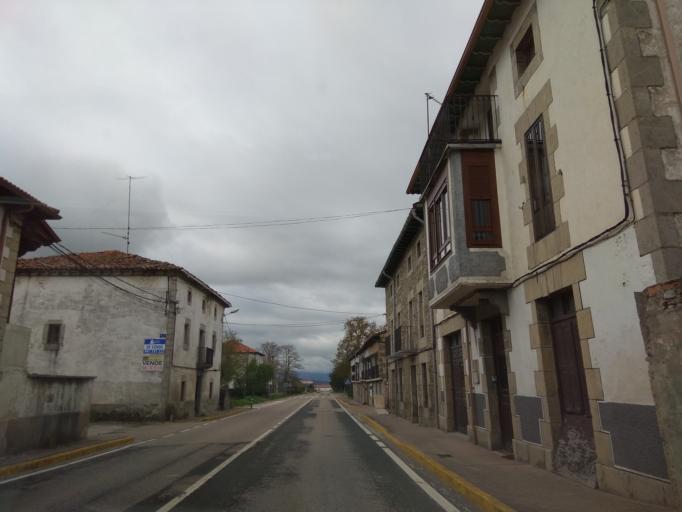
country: ES
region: Castille and Leon
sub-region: Provincia de Burgos
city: Espinosa de los Monteros
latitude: 43.0650
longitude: -3.4743
